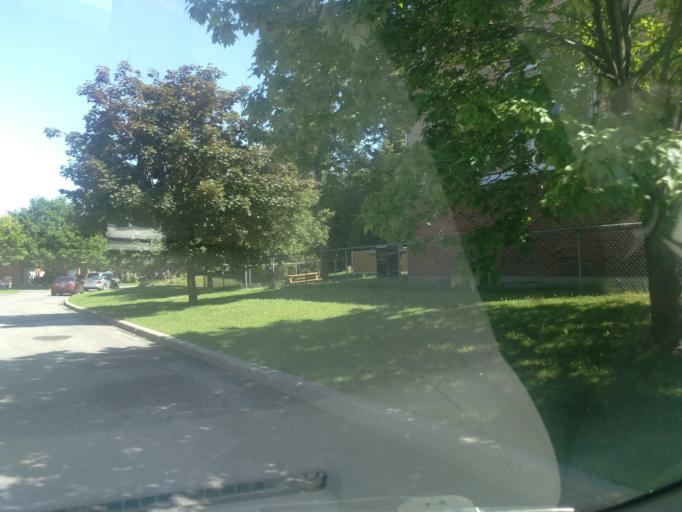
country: CA
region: Quebec
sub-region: Outaouais
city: Gatineau
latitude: 45.4781
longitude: -75.5248
